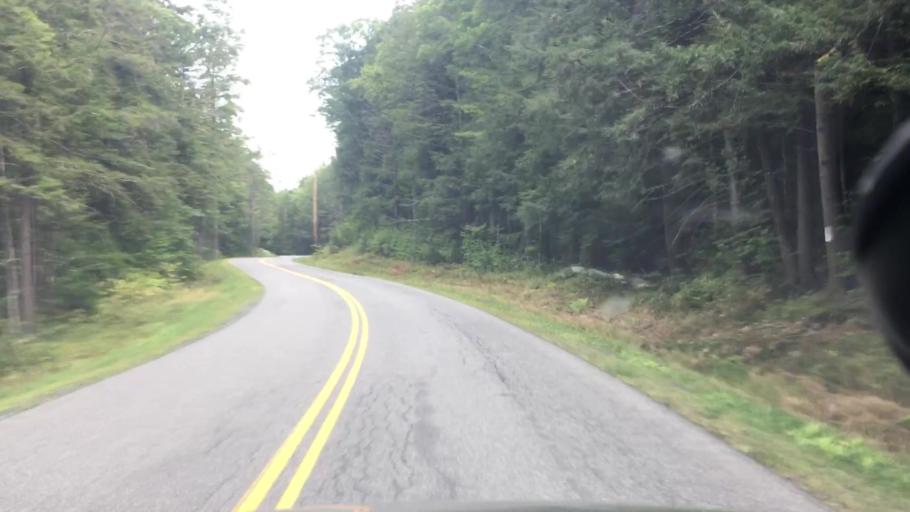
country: US
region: Vermont
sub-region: Windham County
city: Dover
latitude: 42.8095
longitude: -72.7657
